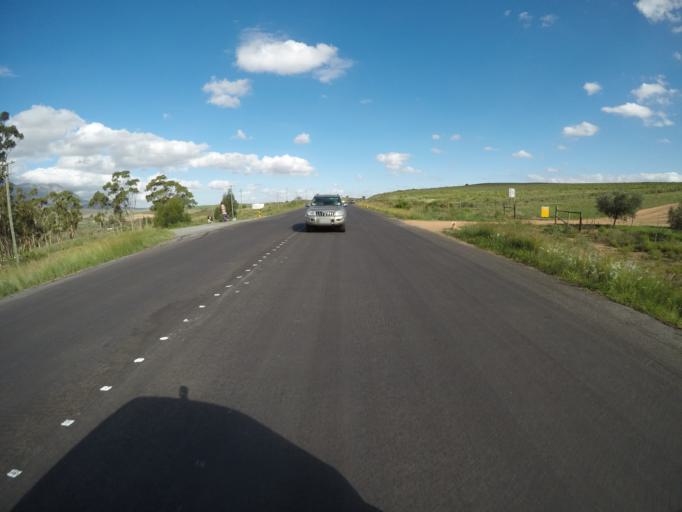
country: ZA
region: Western Cape
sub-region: Cape Winelands District Municipality
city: Ashton
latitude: -33.9392
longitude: 20.2143
